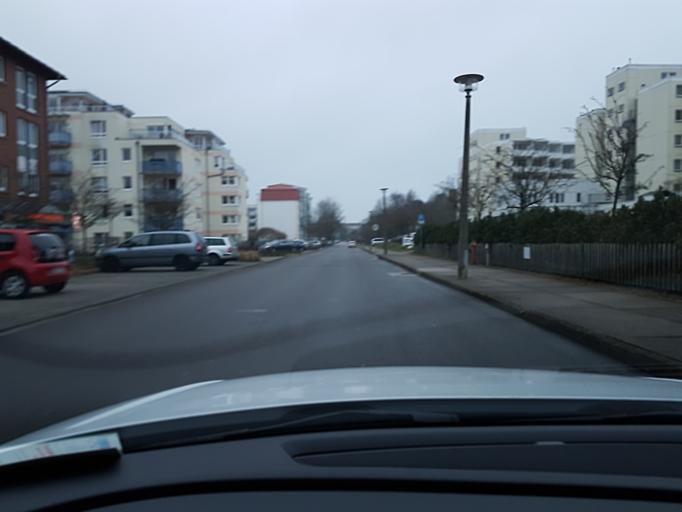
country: DE
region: Mecklenburg-Vorpommern
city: Ostseebad Binz
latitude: 54.4075
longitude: 13.6024
